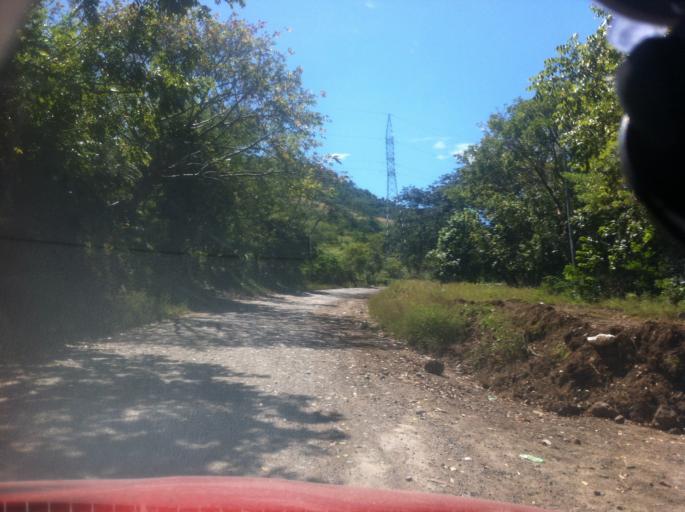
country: NI
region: Matagalpa
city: San Ramon
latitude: 12.8598
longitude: -85.8287
